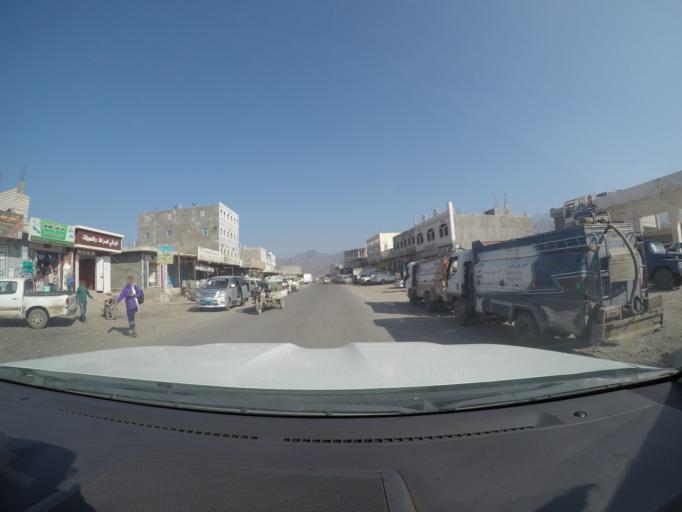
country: YE
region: Lahij
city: Habil ar Raydah
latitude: 13.6447
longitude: 44.8580
